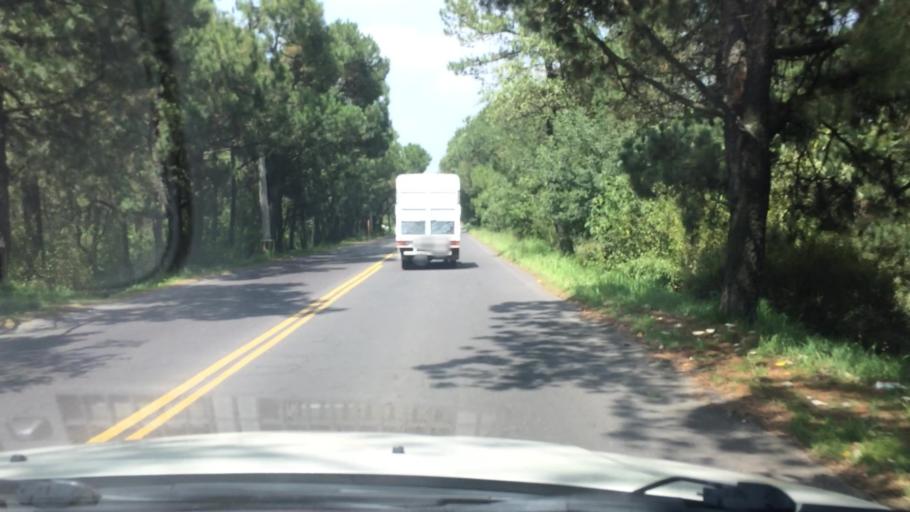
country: MX
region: Mexico City
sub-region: Tlalpan
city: Lomas de Tepemecatl
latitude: 19.2573
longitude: -99.2424
